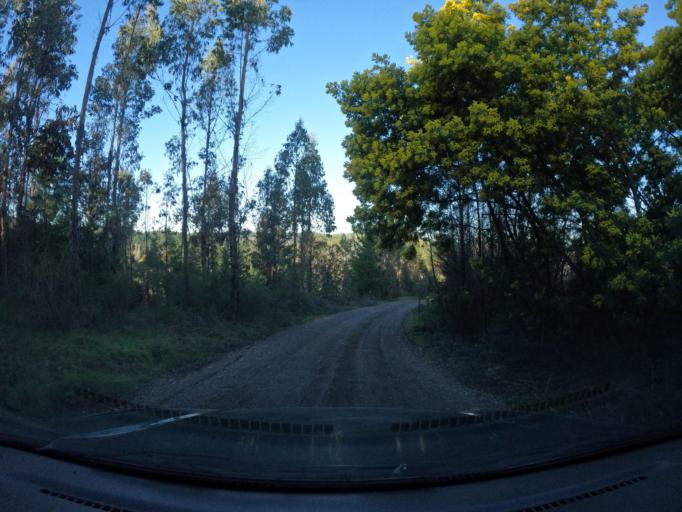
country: CL
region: Biobio
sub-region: Provincia de Concepcion
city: Chiguayante
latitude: -37.0157
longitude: -72.8374
